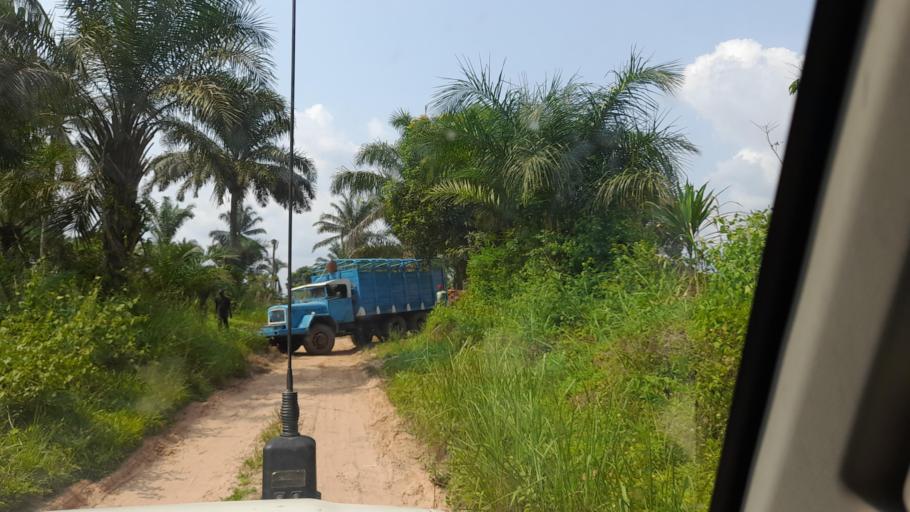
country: CD
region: Kasai-Occidental
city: Kananga
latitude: -5.9177
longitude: 22.4780
